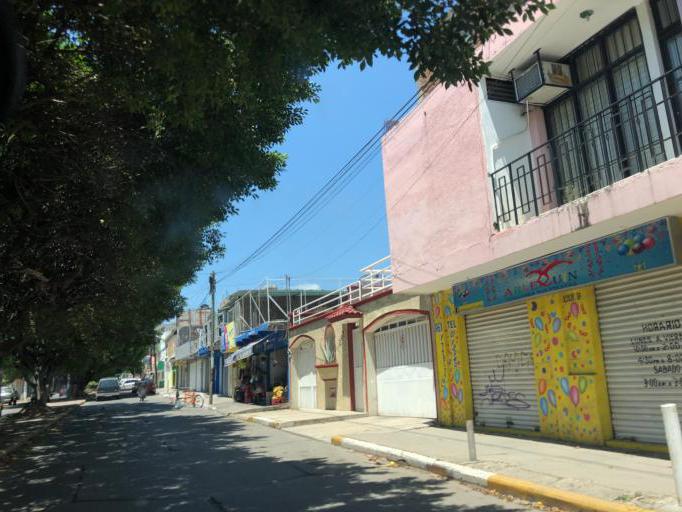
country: MX
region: Chiapas
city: Tuxtla Gutierrez
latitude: 16.7571
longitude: -93.1253
